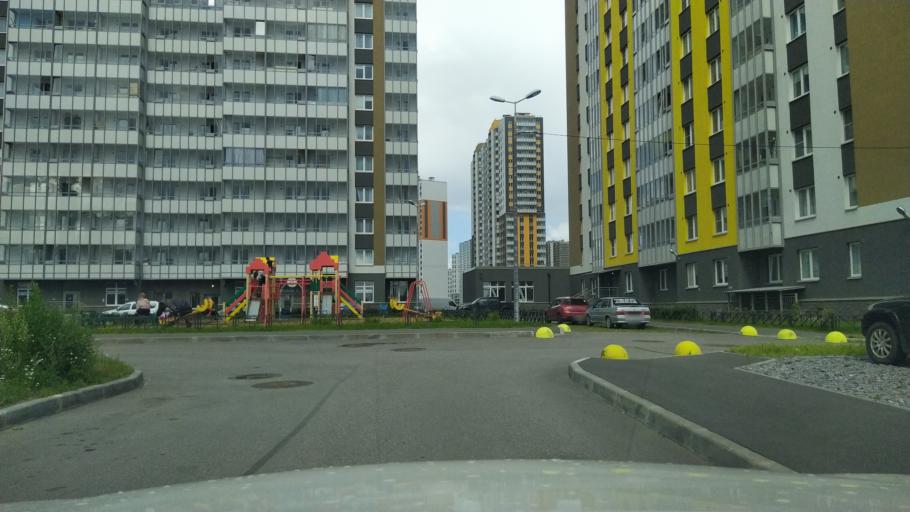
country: RU
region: St.-Petersburg
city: Krasnogvargeisky
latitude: 60.0071
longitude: 30.4823
